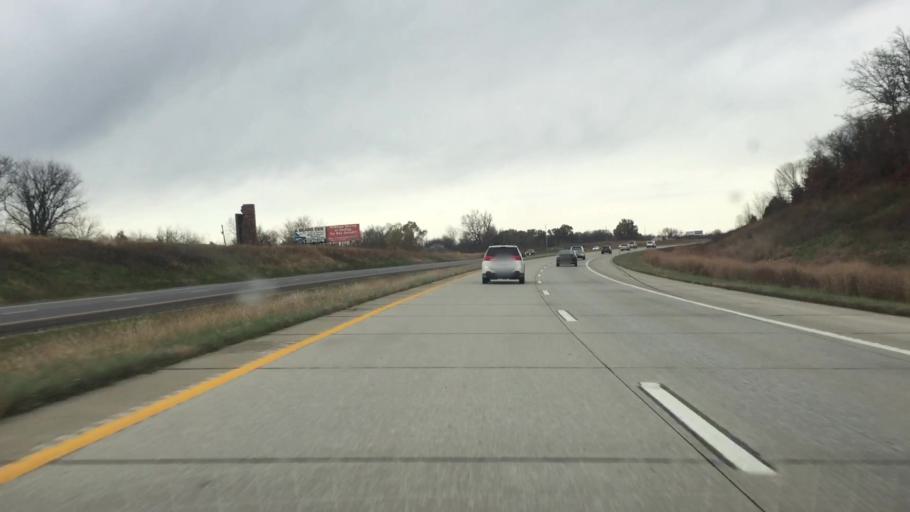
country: US
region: Missouri
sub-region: Saint Clair County
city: Osceola
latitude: 38.0862
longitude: -93.7073
